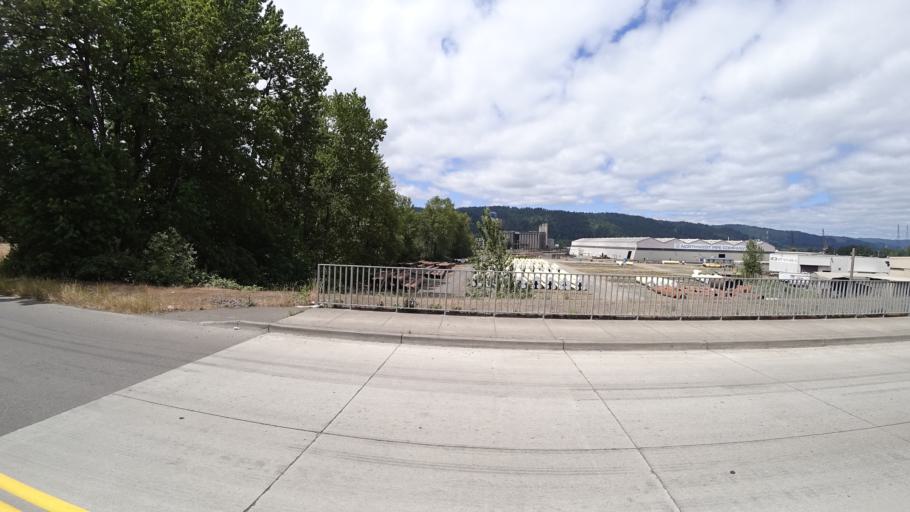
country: US
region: Oregon
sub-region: Washington County
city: West Haven
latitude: 45.6075
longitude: -122.7670
